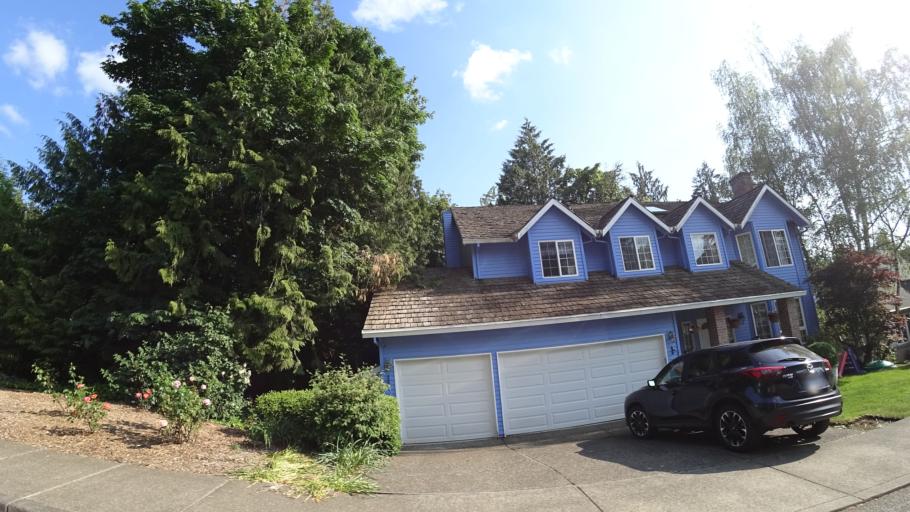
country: US
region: Oregon
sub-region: Washington County
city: Garden Home-Whitford
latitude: 45.4616
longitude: -122.7376
